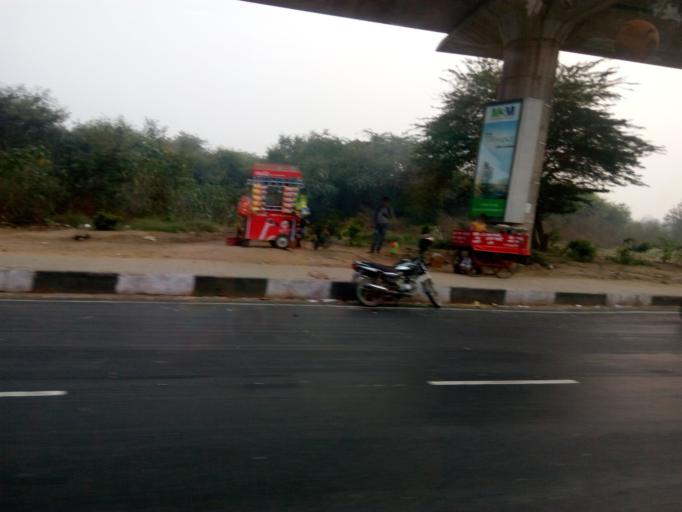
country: IN
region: NCT
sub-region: Central Delhi
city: Karol Bagh
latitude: 28.5907
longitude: 77.1582
